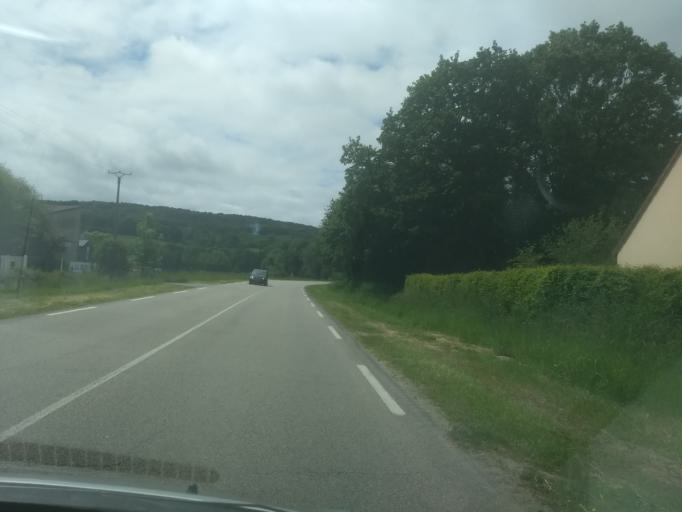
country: FR
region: Lower Normandy
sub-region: Departement de l'Orne
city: Remalard
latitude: 48.4255
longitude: 0.7844
